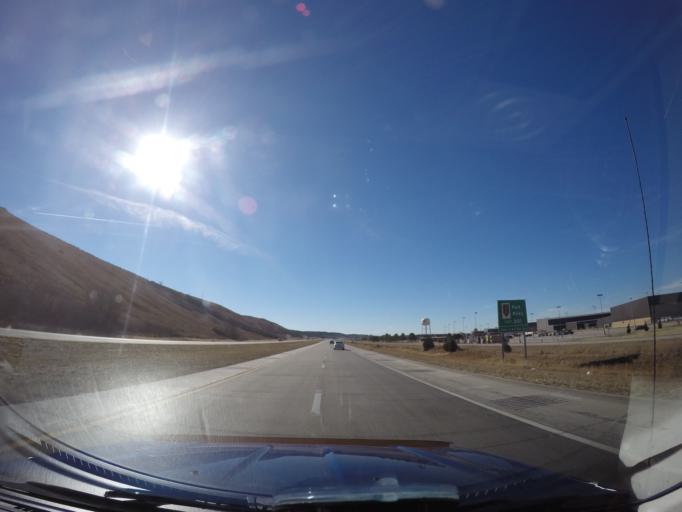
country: US
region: Kansas
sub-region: Geary County
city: Grandview Plaza
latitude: 39.0517
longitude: -96.7553
